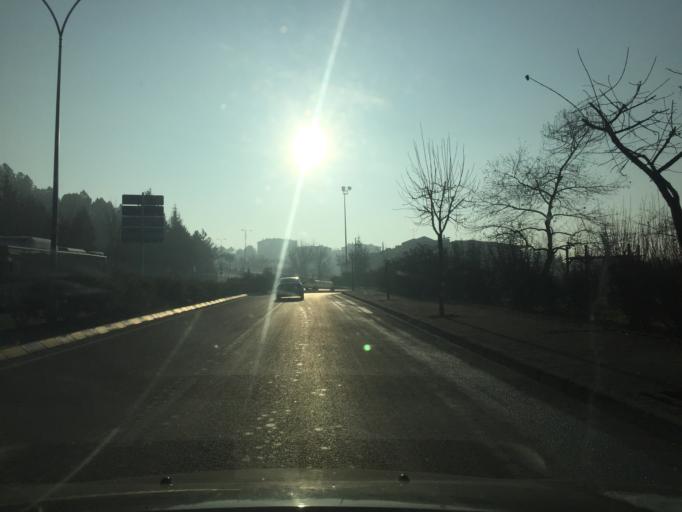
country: TR
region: Duzce
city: Duzce
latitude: 40.8676
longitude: 31.2302
